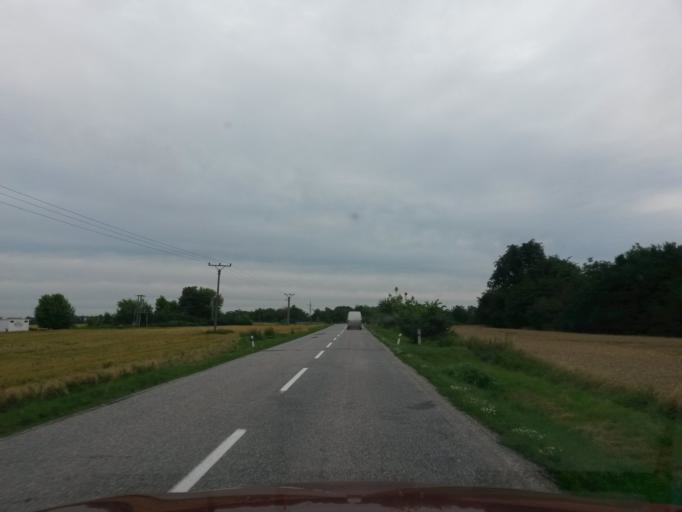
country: SK
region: Nitriansky
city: Levice
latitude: 48.1342
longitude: 18.5923
